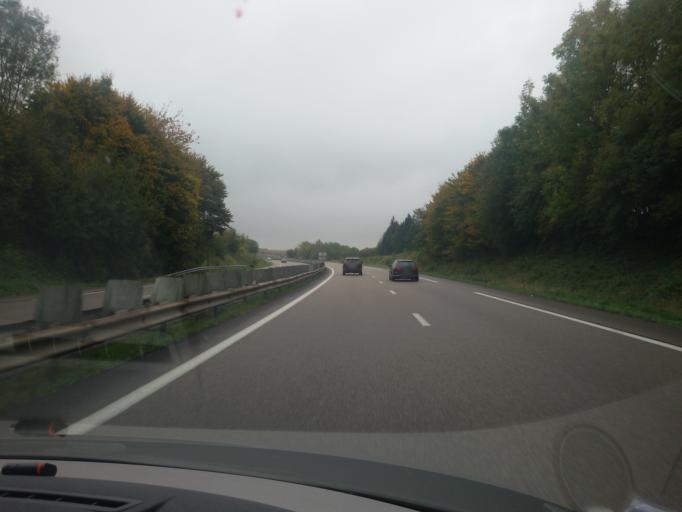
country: FR
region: Haute-Normandie
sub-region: Departement de l'Eure
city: Beuzeville
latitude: 49.3326
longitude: 0.3911
